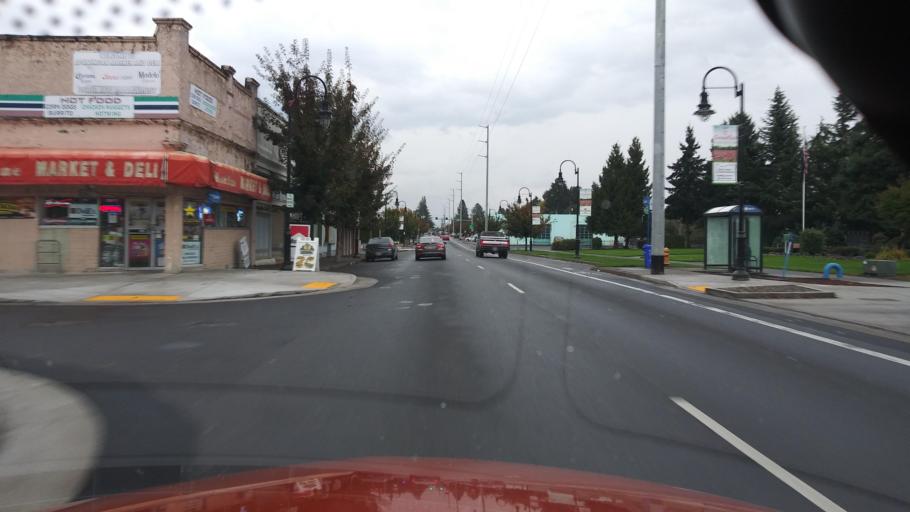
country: US
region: Oregon
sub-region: Washington County
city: Cornelius
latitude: 45.5201
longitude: -123.0573
